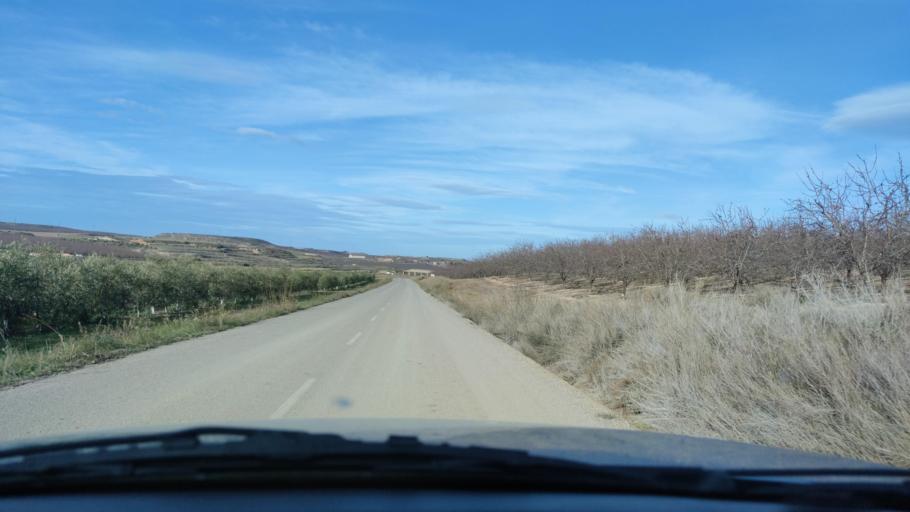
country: ES
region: Catalonia
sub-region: Provincia de Lleida
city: Alcano
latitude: 41.4714
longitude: 0.6328
